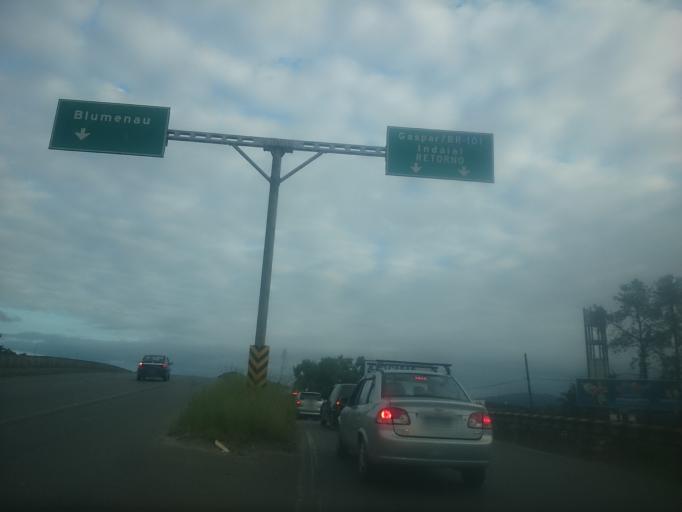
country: BR
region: Santa Catarina
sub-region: Blumenau
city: Blumenau
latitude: -26.8609
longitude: -49.0860
